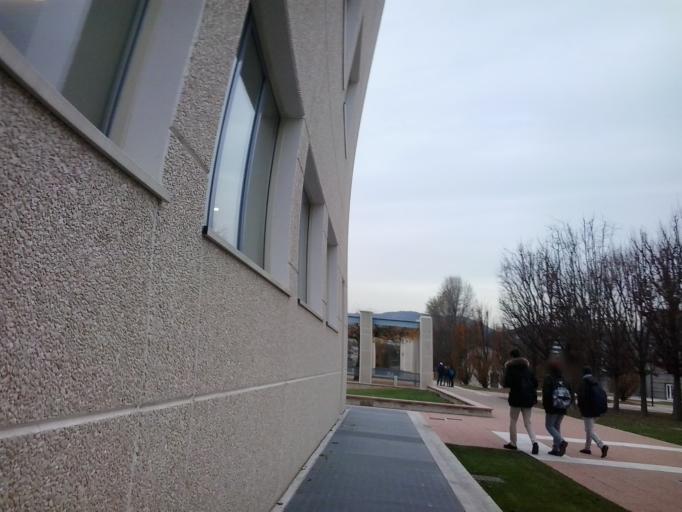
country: IT
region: Lombardy
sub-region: Provincia di Brescia
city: Bovezzo
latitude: 45.5648
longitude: 10.2332
